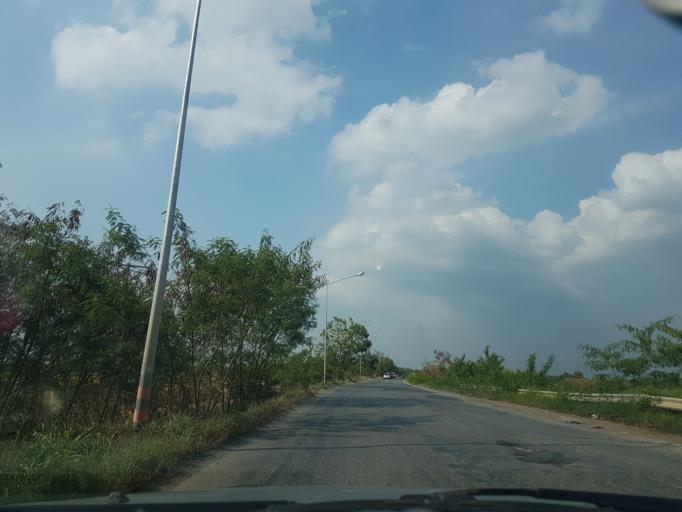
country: TH
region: Phra Nakhon Si Ayutthaya
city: Phachi
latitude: 14.4062
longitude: 100.7867
